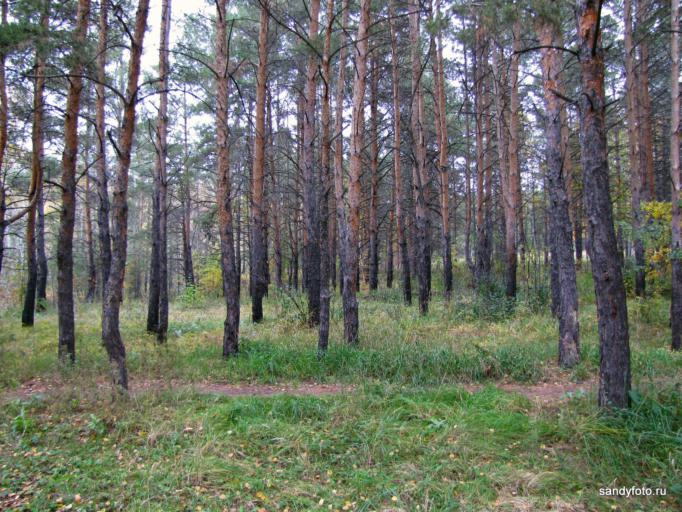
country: RU
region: Chelyabinsk
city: Troitsk
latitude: 54.0566
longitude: 61.6274
